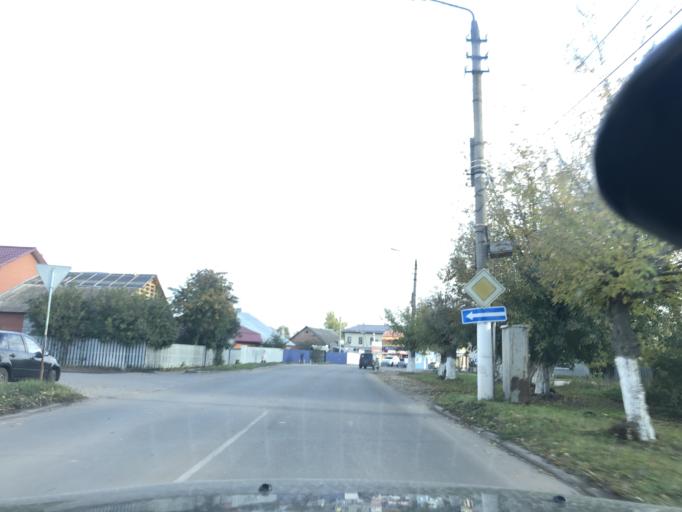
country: RU
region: Tula
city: Kireyevsk
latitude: 53.9317
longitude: 37.9263
